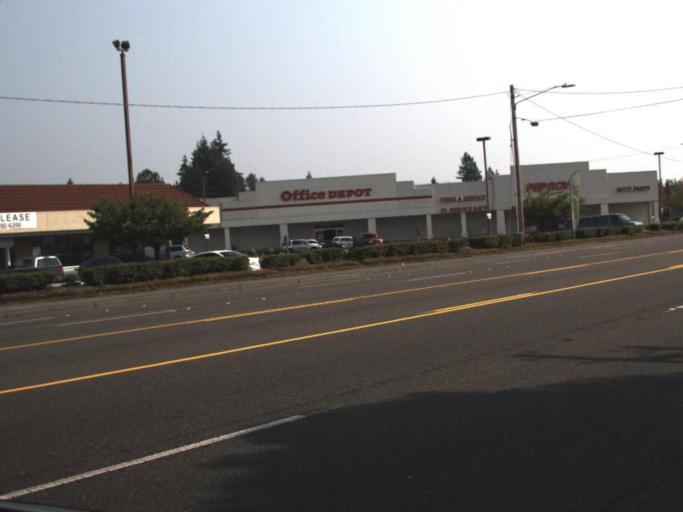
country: US
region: Washington
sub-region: Snohomish County
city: Martha Lake
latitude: 47.9047
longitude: -122.2416
